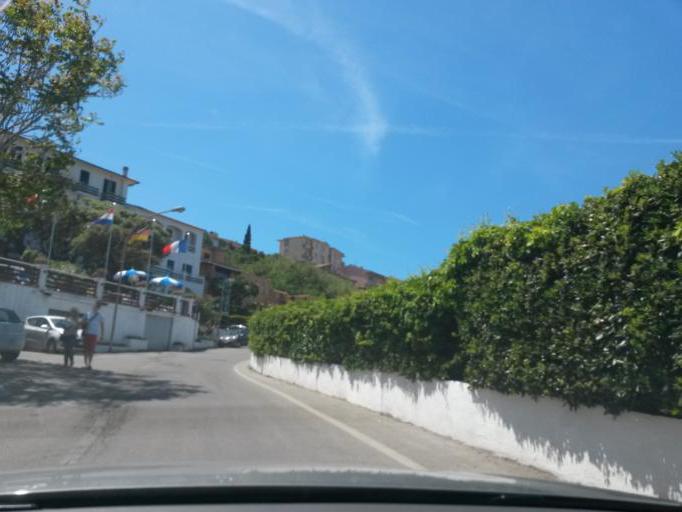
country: IT
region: Tuscany
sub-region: Provincia di Livorno
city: Portoferraio
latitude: 42.8170
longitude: 10.3225
